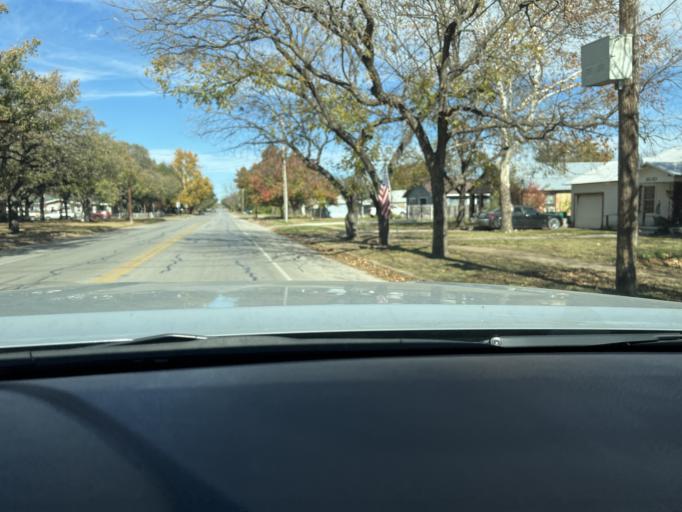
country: US
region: Texas
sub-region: Eastland County
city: Eastland
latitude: 32.3917
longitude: -98.8181
